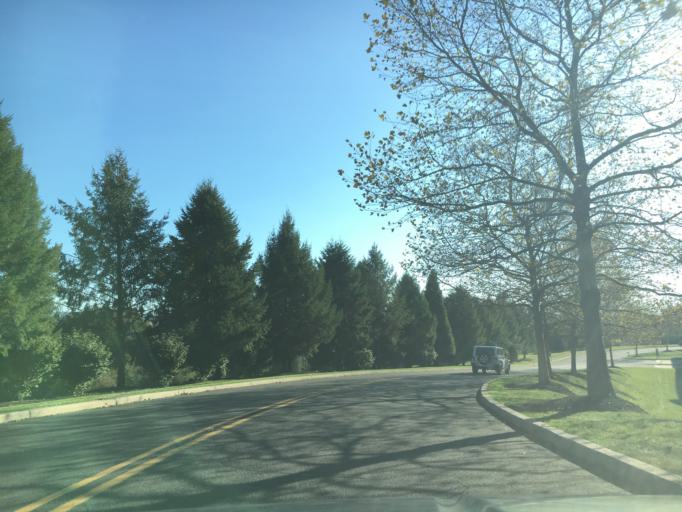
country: US
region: Pennsylvania
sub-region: Lehigh County
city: Fullerton
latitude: 40.6319
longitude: -75.4528
